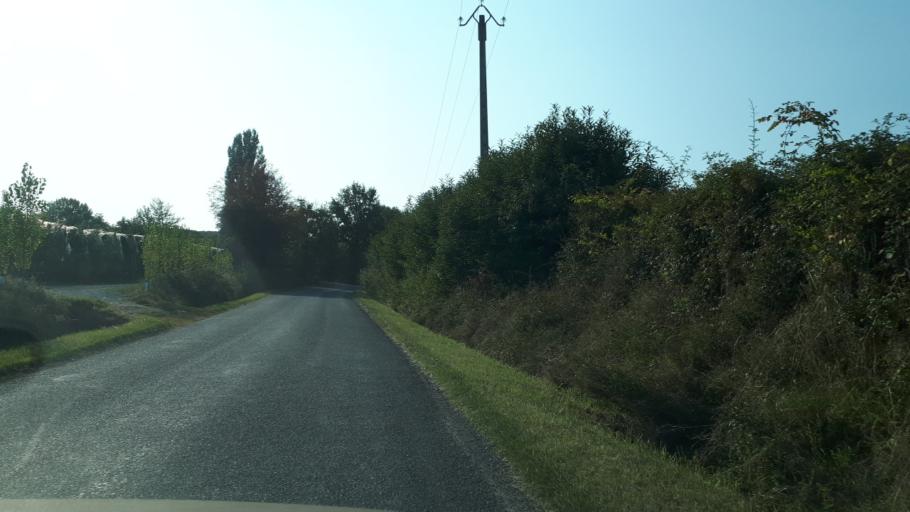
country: FR
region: Centre
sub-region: Departement du Cher
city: Vasselay
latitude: 47.2157
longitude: 2.3773
